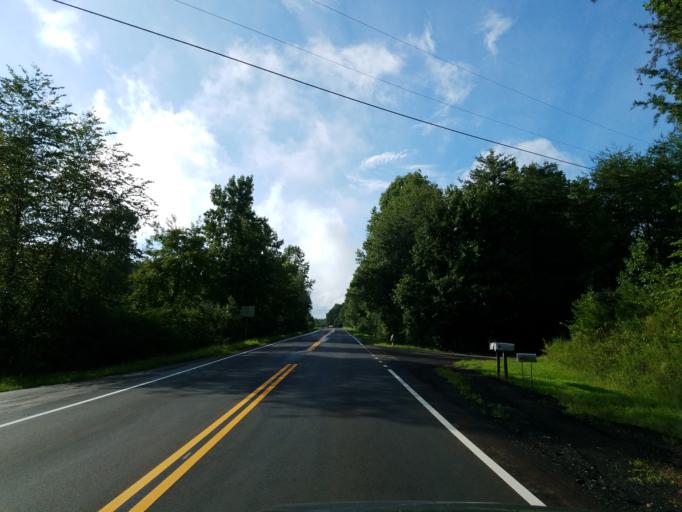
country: US
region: Georgia
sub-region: White County
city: Cleveland
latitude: 34.6182
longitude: -83.7978
